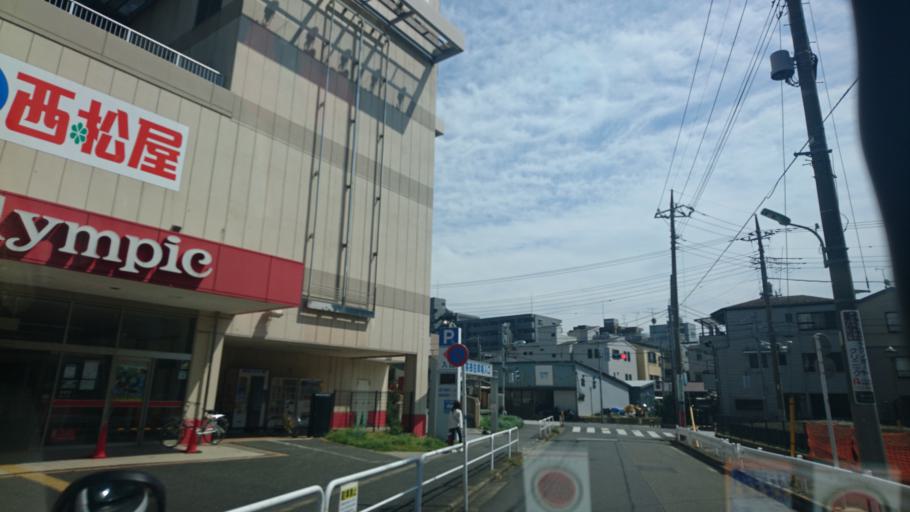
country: JP
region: Kanagawa
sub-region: Kawasaki-shi
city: Kawasaki
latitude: 35.5465
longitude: 139.7263
